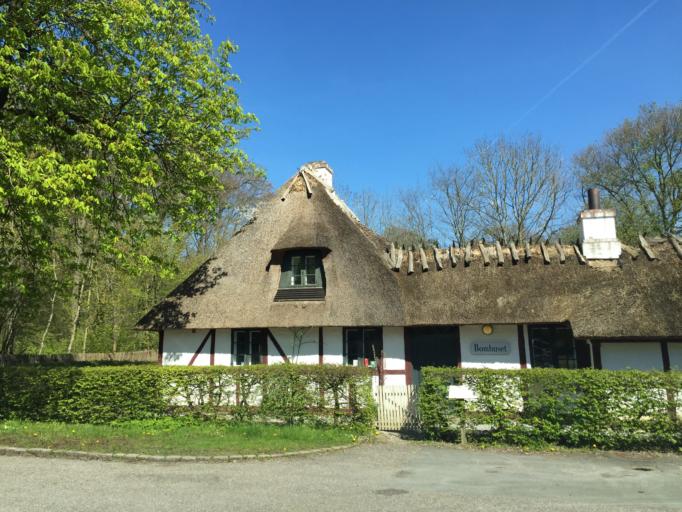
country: DK
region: South Denmark
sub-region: Odense Kommune
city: Odense
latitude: 55.3670
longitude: 10.3841
